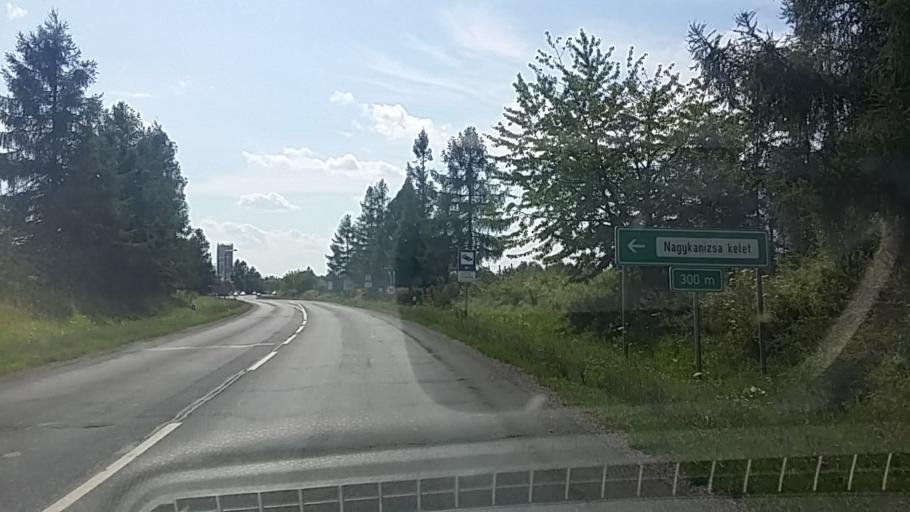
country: HU
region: Zala
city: Nagykanizsa
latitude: 46.4664
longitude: 17.0114
